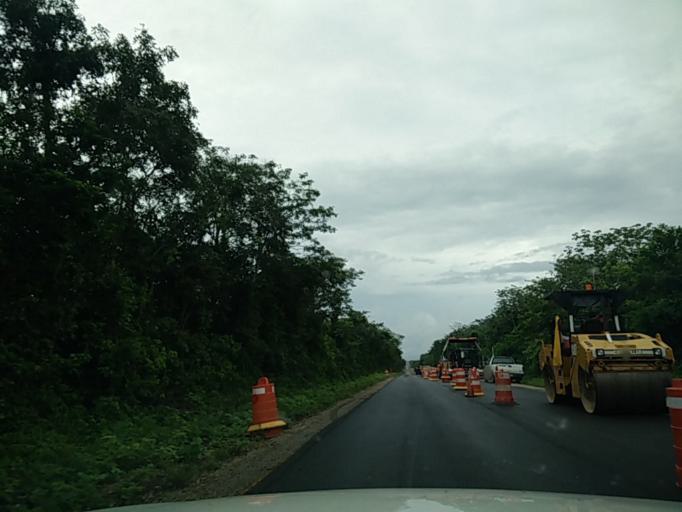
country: MX
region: Quintana Roo
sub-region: Lazaro Cardenas
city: El Tintal
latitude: 20.8981
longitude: -87.4808
